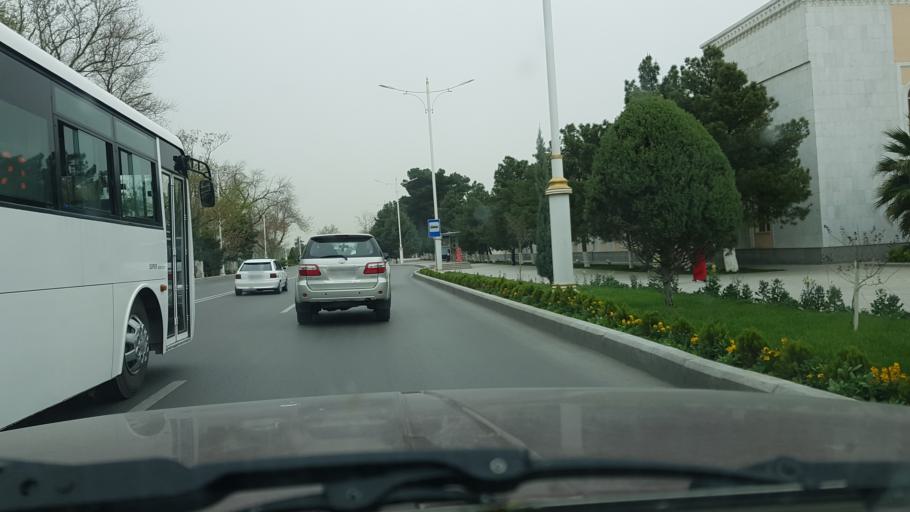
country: TM
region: Ahal
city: Ashgabat
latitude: 37.9503
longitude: 58.3448
